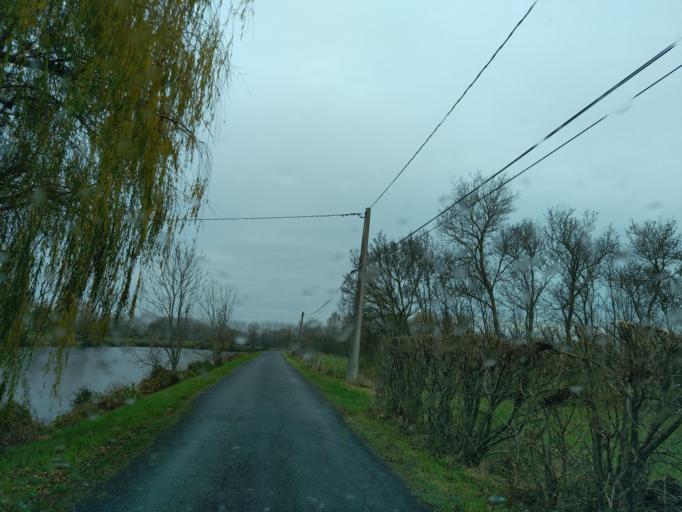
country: FR
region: Pays de la Loire
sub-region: Departement de la Vendee
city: Maillezais
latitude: 46.3192
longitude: -0.7829
